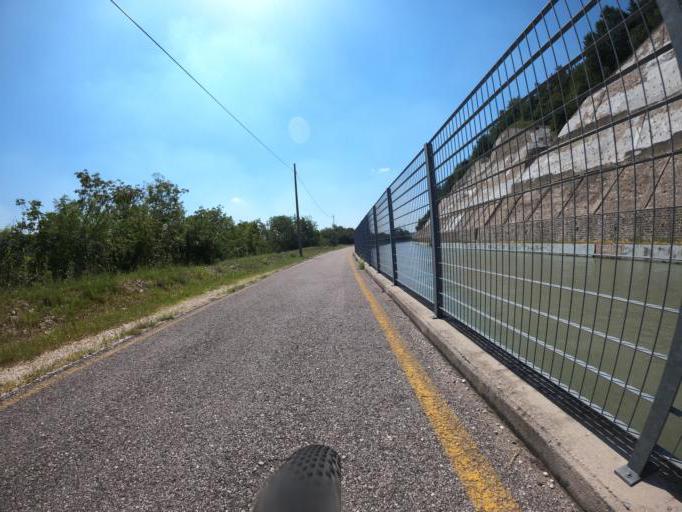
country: IT
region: Veneto
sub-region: Provincia di Verona
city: Volargne
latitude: 45.5492
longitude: 10.8188
